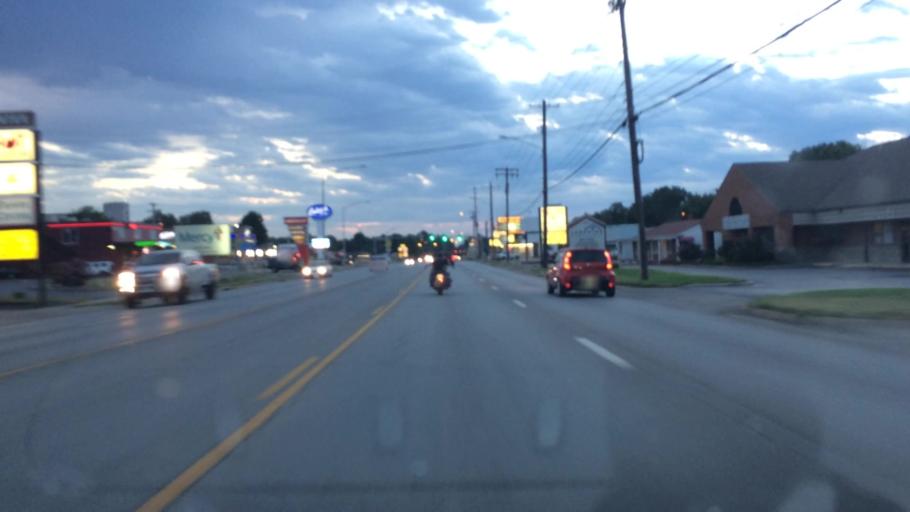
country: US
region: Missouri
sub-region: Greene County
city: Springfield
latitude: 37.1818
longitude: -93.2693
